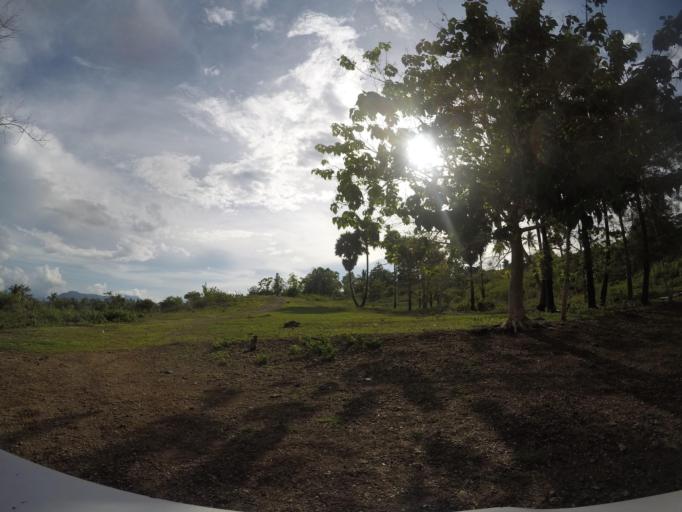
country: TL
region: Baucau
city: Baucau
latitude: -8.5068
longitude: 126.4455
